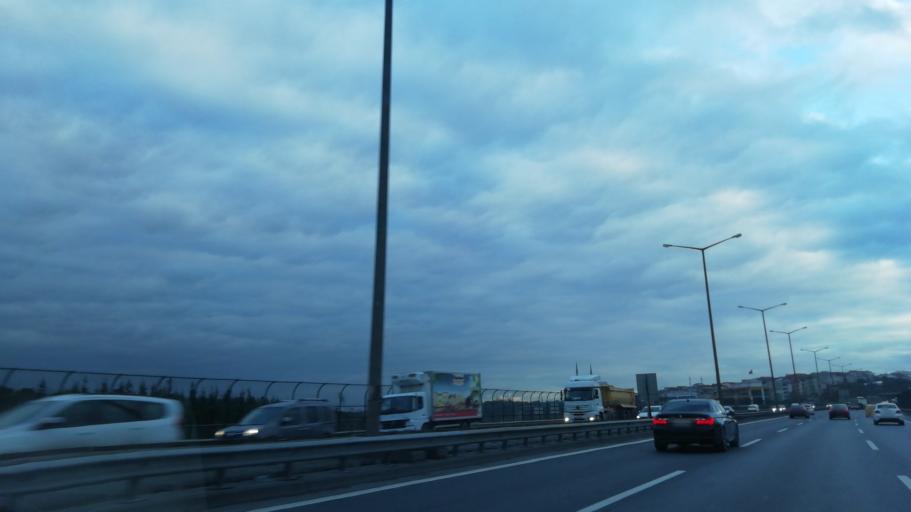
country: TR
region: Istanbul
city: Mahmutbey
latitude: 41.0622
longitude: 28.8469
